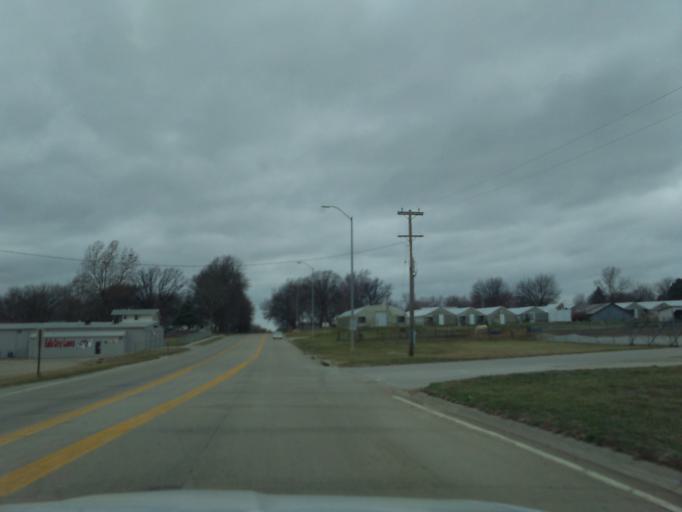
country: US
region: Nebraska
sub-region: Richardson County
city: Falls City
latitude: 40.0584
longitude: -95.5886
